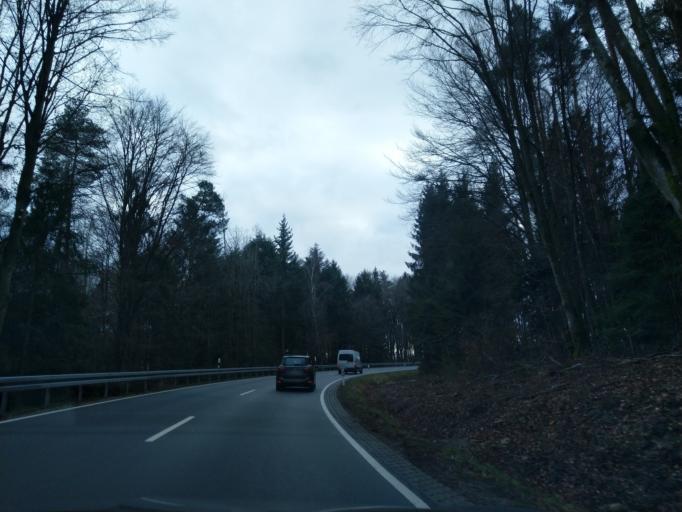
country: DE
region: Bavaria
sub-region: Lower Bavaria
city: Schaufling
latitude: 48.8393
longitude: 13.0629
